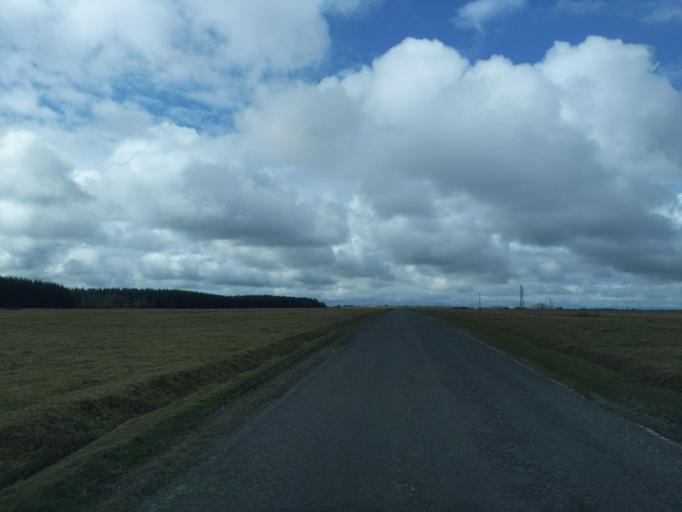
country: GB
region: England
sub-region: Cornwall
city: Camelford
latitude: 50.6336
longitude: -4.6132
